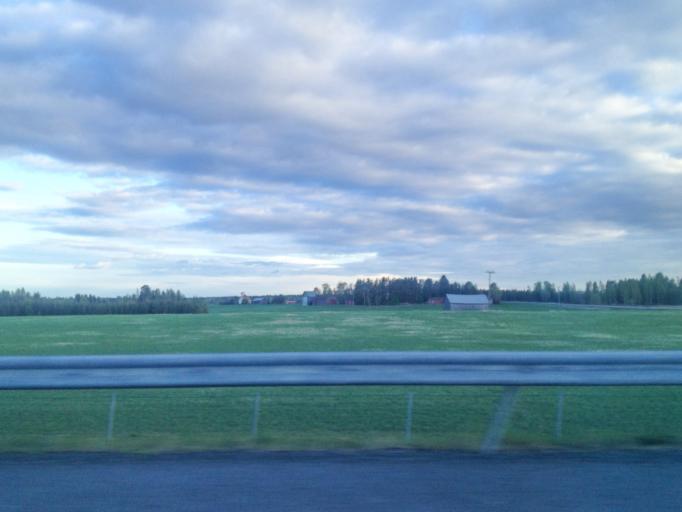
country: FI
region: Haeme
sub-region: Haemeenlinna
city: Kalvola
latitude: 61.1427
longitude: 24.0200
